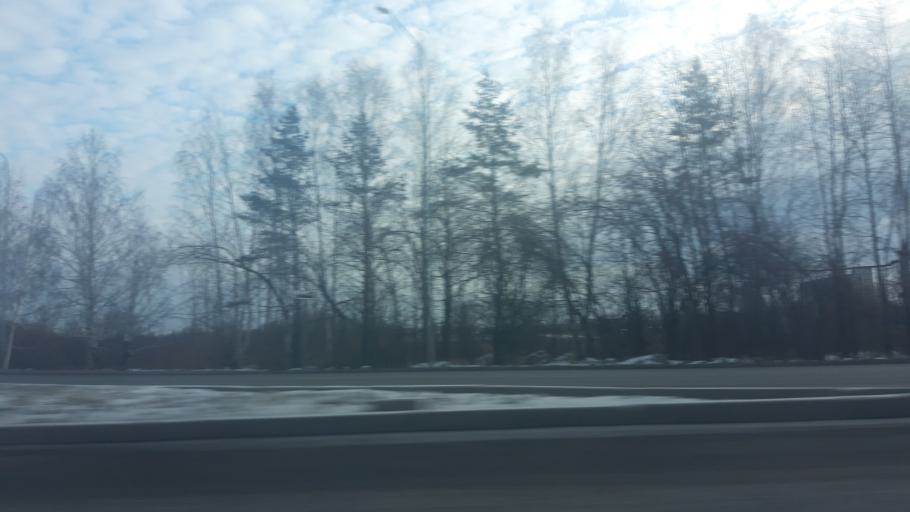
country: RU
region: Tjumen
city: Moskovskiy
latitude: 57.1857
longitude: 65.3564
